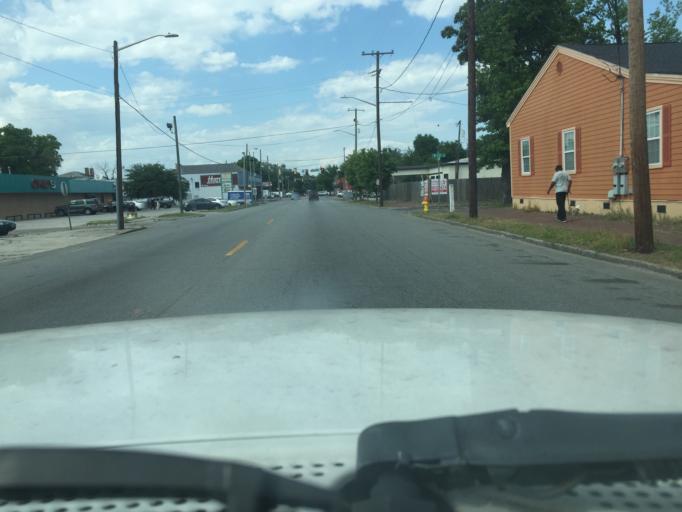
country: US
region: Georgia
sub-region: Chatham County
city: Savannah
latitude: 32.0624
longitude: -81.1028
